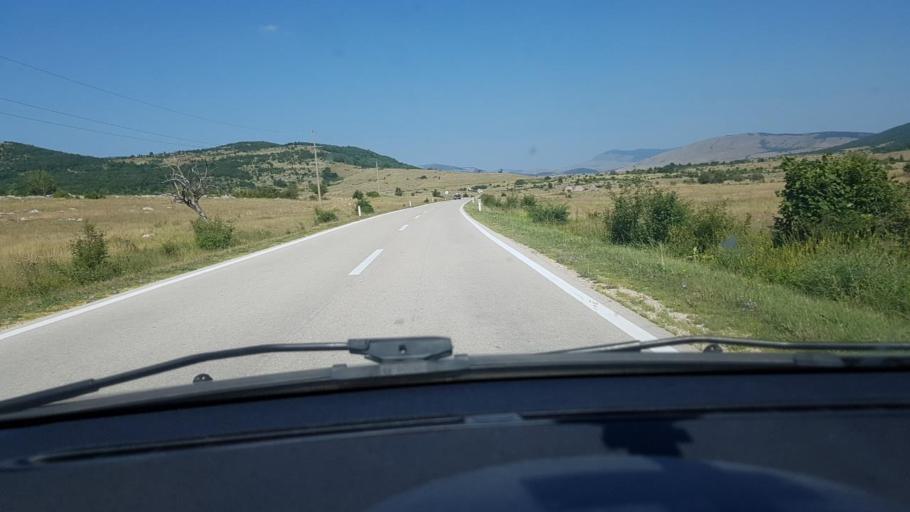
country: BA
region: Federation of Bosnia and Herzegovina
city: Bosansko Grahovo
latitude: 44.1314
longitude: 16.4884
